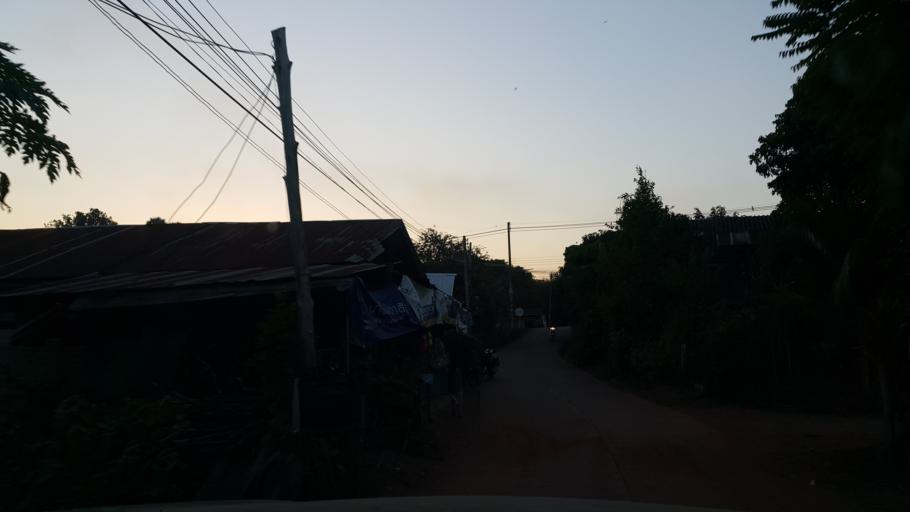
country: TH
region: Phrae
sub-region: Amphoe Wang Chin
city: Wang Chin
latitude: 17.8749
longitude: 99.6200
